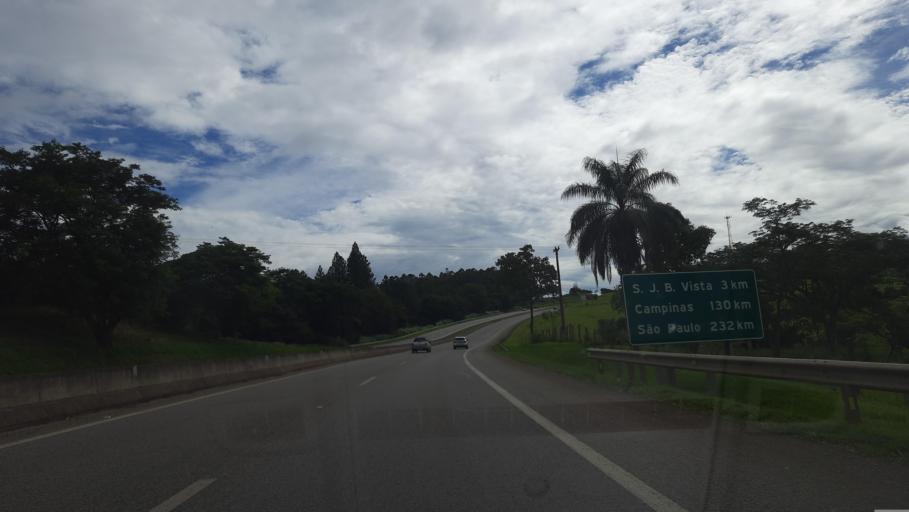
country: BR
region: Sao Paulo
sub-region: Sao Joao Da Boa Vista
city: Sao Joao da Boa Vista
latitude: -21.9696
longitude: -46.7416
